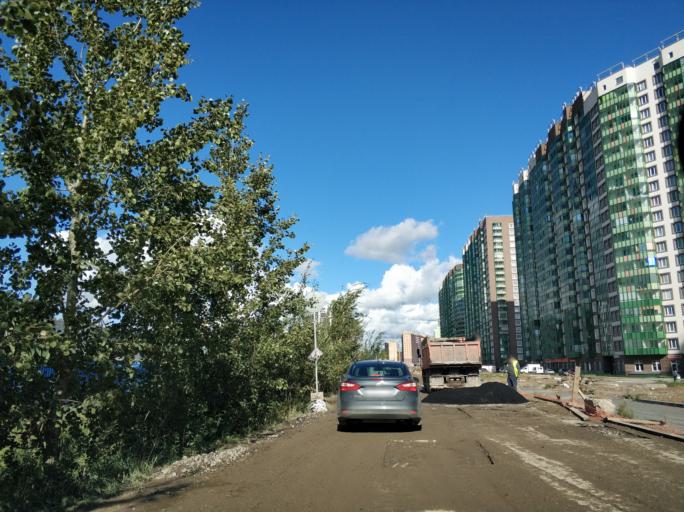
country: RU
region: St.-Petersburg
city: Grazhdanka
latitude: 60.0542
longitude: 30.4202
